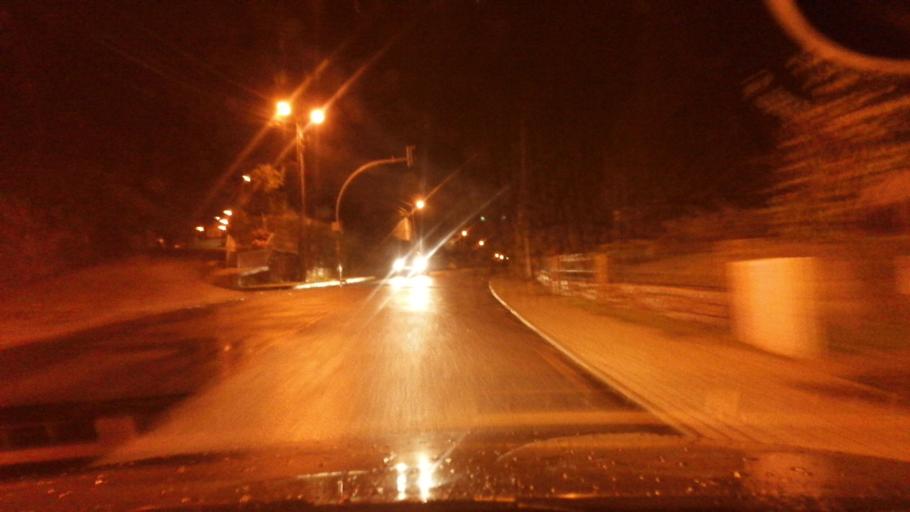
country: PT
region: Viseu
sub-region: Moimenta da Beira
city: Moimenta da Beira
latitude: 40.9462
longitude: -7.5737
